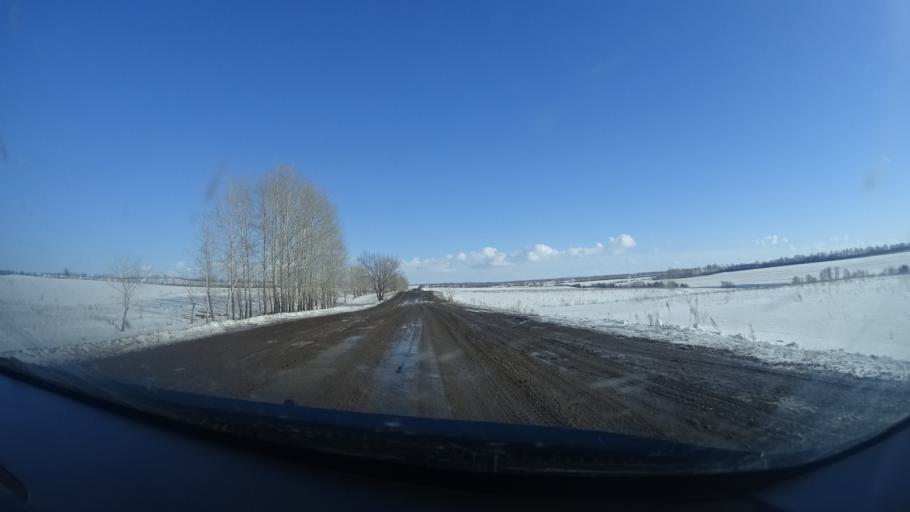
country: RU
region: Bashkortostan
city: Chishmy
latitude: 54.6014
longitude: 55.2221
